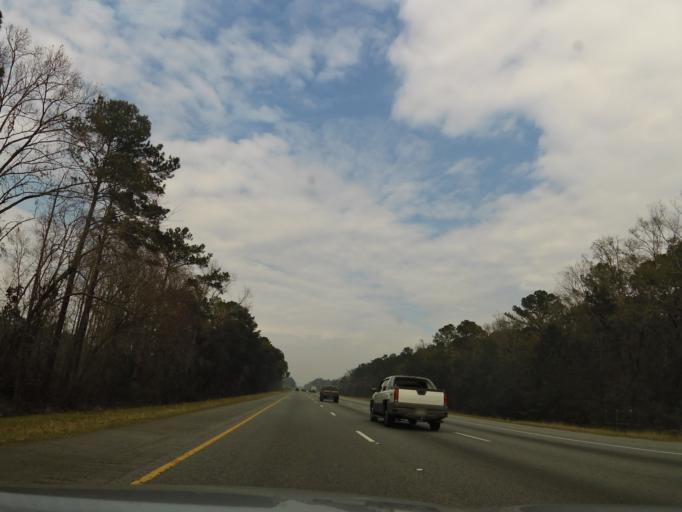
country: US
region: Georgia
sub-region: Liberty County
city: Midway
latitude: 31.7089
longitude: -81.3902
